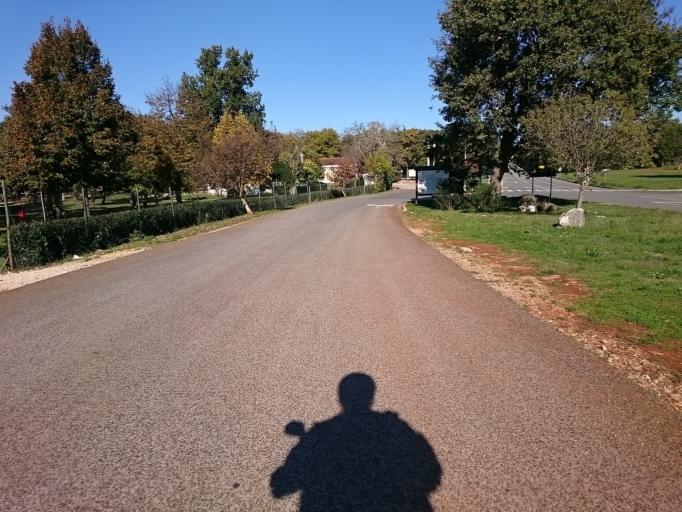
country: HR
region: Istarska
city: Umag
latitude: 45.3918
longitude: 13.5420
